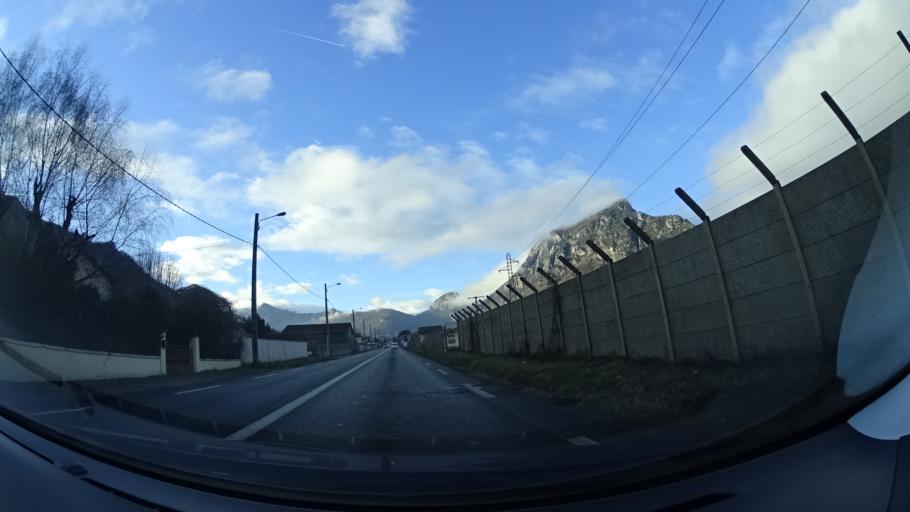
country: FR
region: Midi-Pyrenees
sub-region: Departement de l'Ariege
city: Tarascon-sur-Ariege
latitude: 42.8506
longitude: 1.5975
